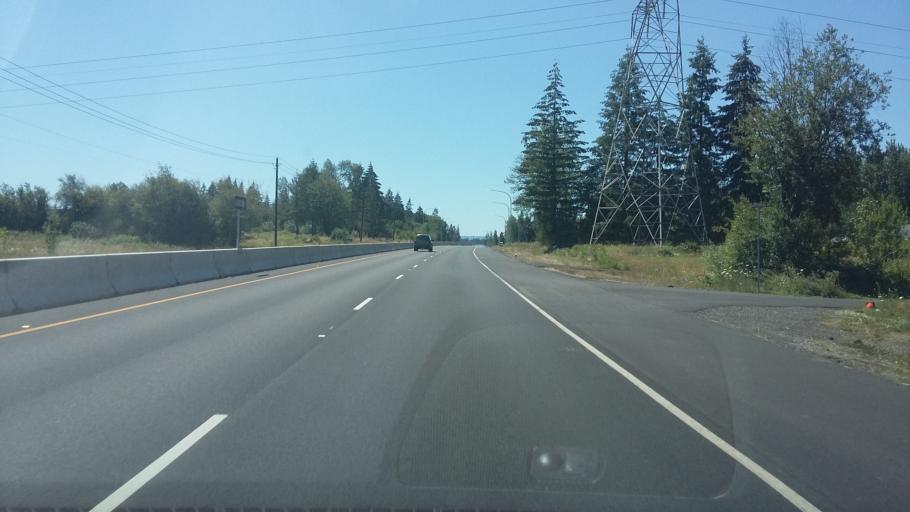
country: US
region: Washington
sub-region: Clark County
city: Dollar Corner
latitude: 45.7798
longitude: -122.6291
